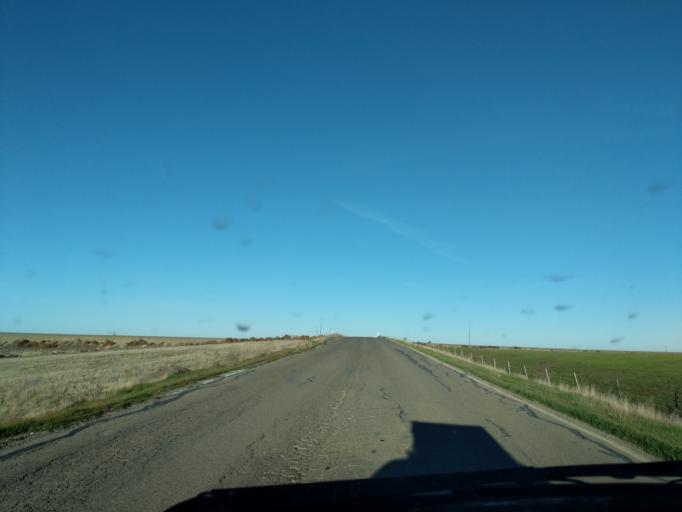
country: US
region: California
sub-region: Merced County
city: Los Banos
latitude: 37.0496
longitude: -120.9573
